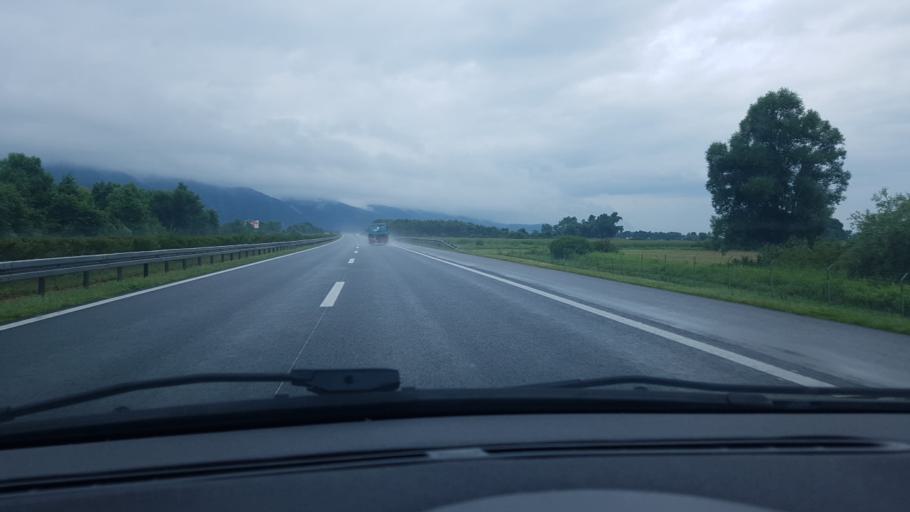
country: HR
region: Zagrebacka
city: Pojatno
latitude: 45.8963
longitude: 15.8222
